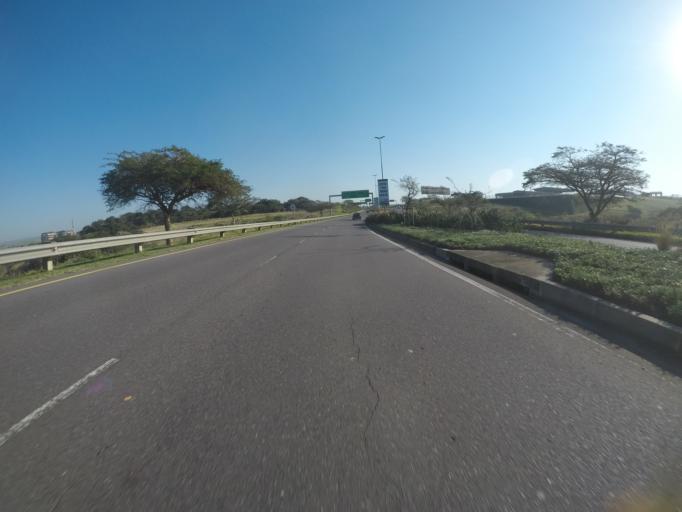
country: ZA
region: KwaZulu-Natal
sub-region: iLembe District Municipality
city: Ballitoville
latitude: -29.6262
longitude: 31.1021
